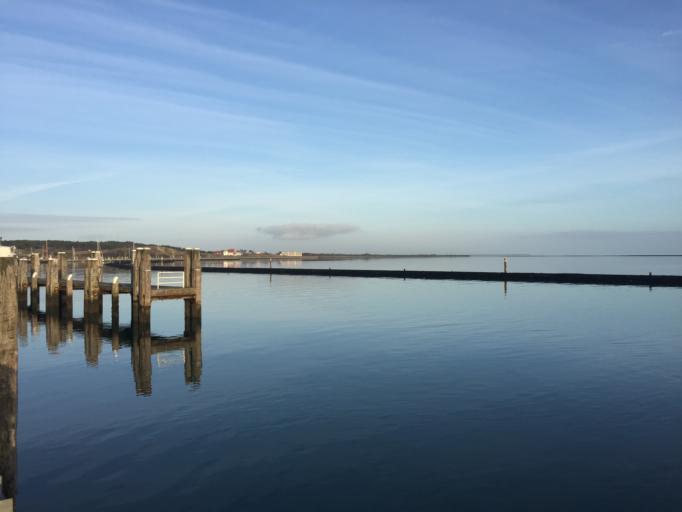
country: NL
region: Friesland
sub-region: Gemeente Terschelling
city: West-Terschelling
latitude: 53.3600
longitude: 5.2173
